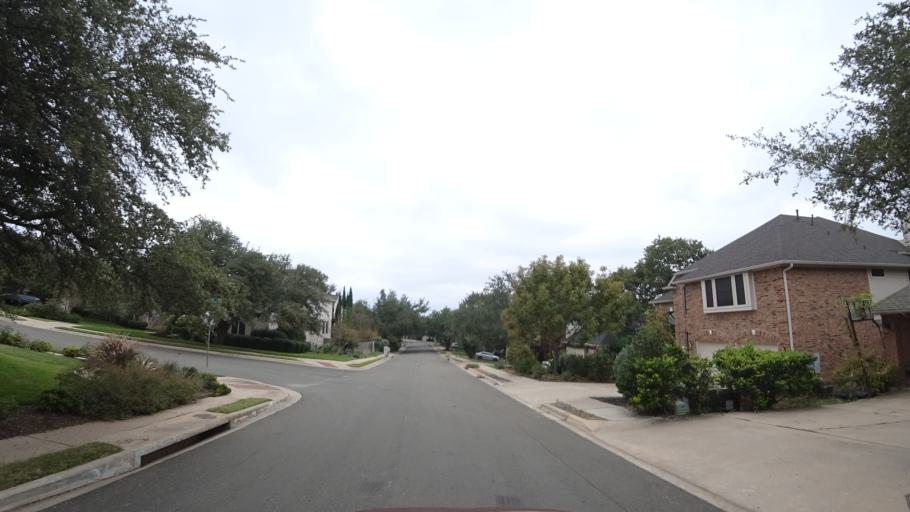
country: US
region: Texas
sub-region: Williamson County
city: Anderson Mill
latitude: 30.4326
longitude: -97.8292
